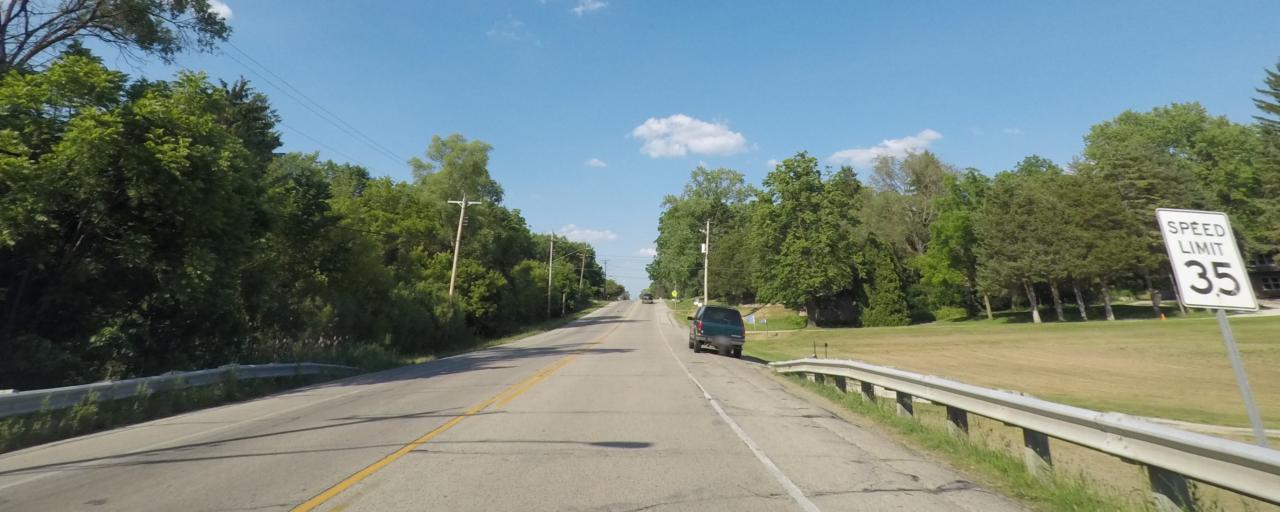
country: US
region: Wisconsin
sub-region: Waukesha County
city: Big Bend
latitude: 42.8799
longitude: -88.2054
